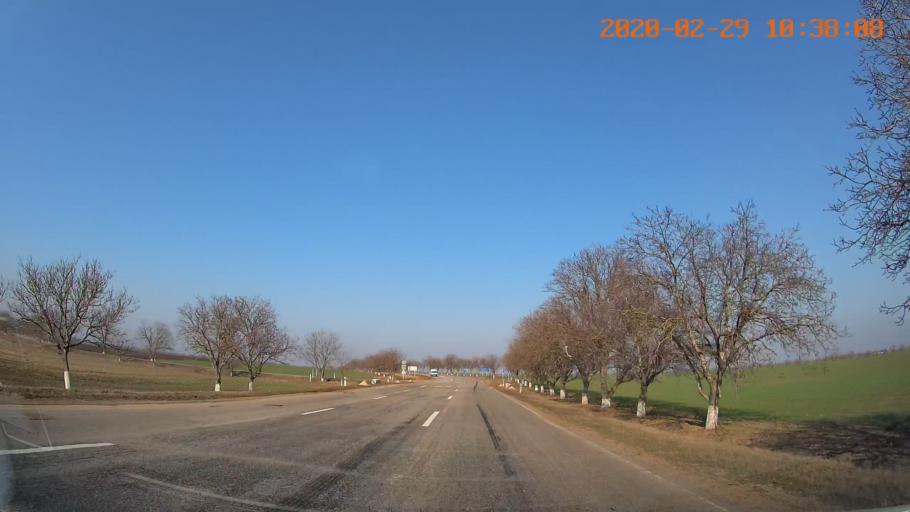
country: MD
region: Anenii Noi
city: Varnita
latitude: 47.0137
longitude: 29.4782
